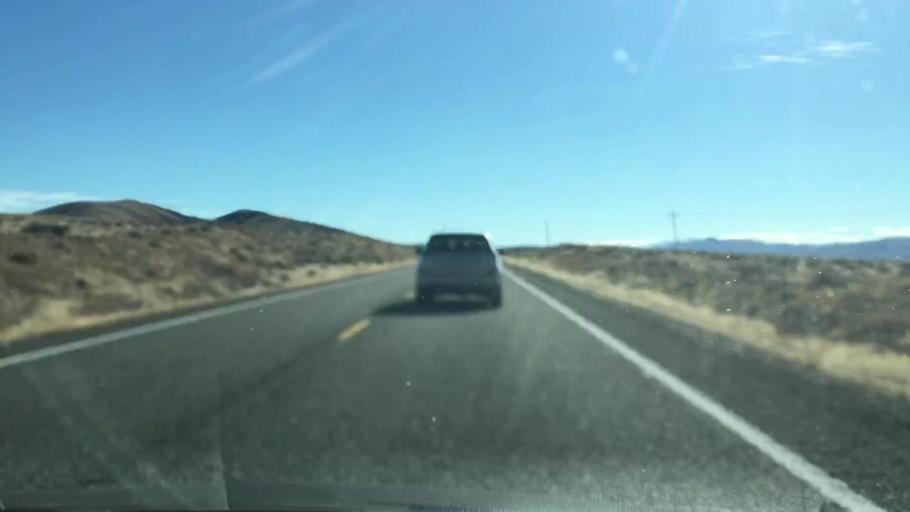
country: US
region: Nevada
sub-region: Lyon County
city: Silver Springs
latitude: 39.2000
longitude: -119.2134
